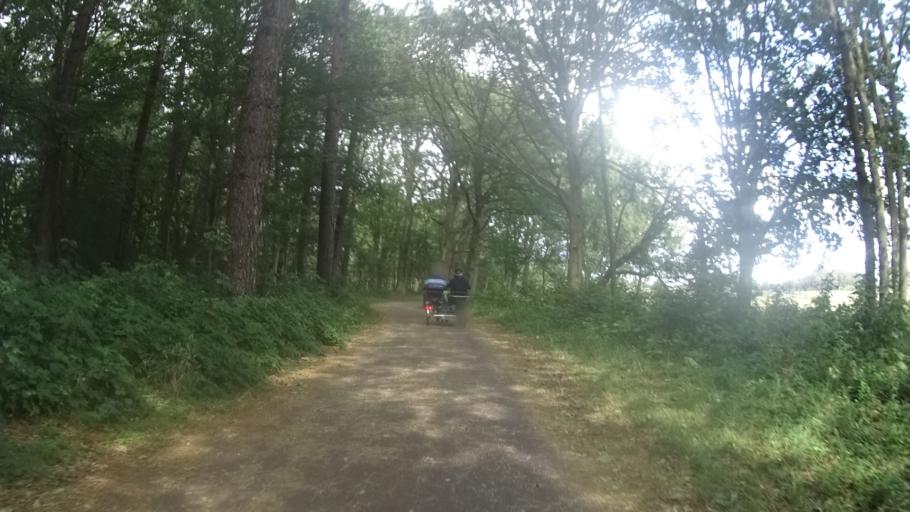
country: NL
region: North Holland
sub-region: Gemeente Bergen
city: Egmond aan Zee
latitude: 52.5950
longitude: 4.6372
